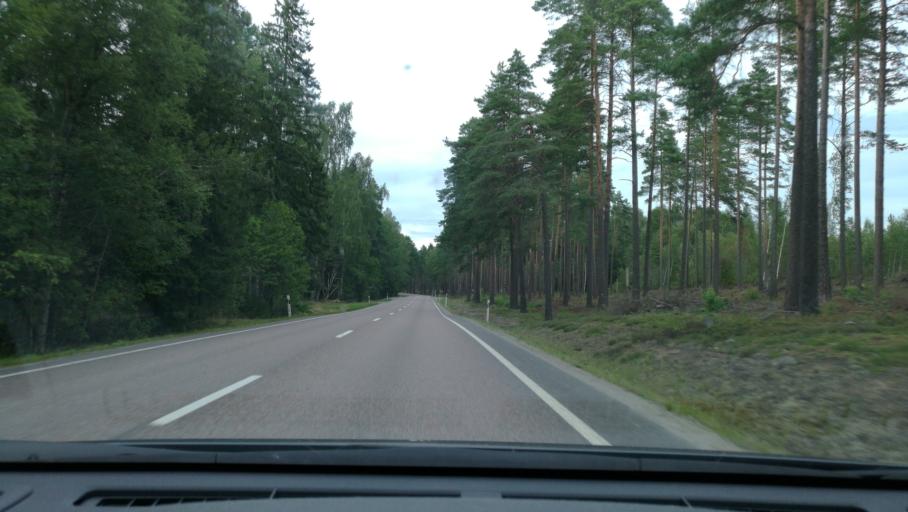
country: SE
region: Vaestmanland
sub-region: Kungsors Kommun
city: Kungsoer
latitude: 59.3847
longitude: 16.1092
